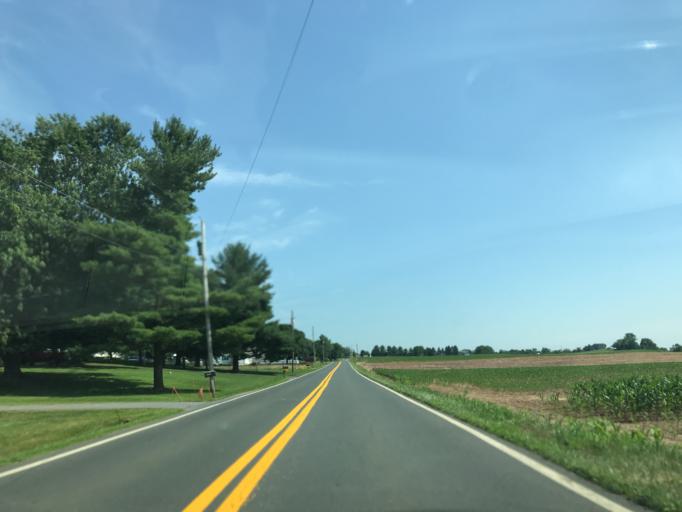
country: US
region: Maryland
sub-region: Carroll County
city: Taneytown
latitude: 39.6160
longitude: -77.1361
